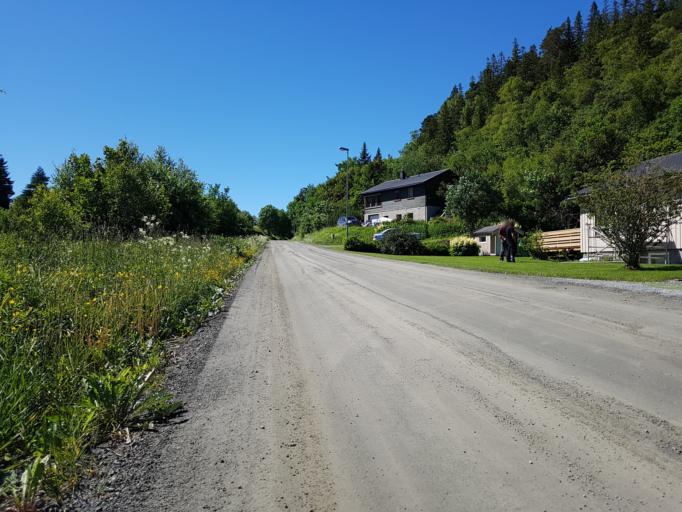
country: NO
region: Sor-Trondelag
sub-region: Skaun
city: Borsa
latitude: 63.4347
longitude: 10.1867
